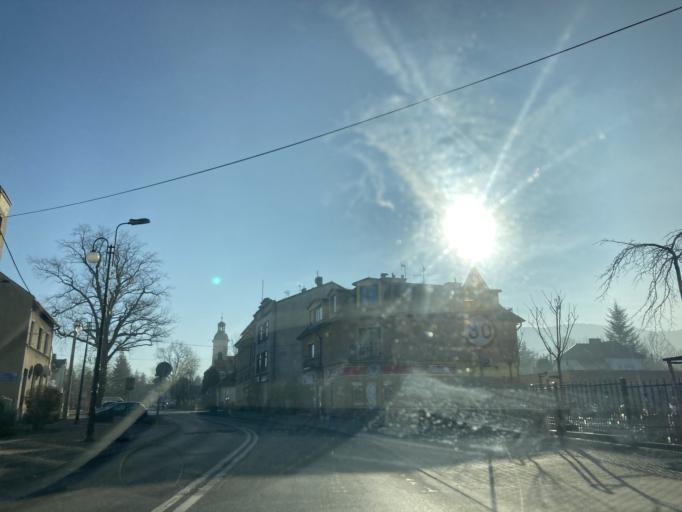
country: PL
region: Silesian Voivodeship
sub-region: Powiat cieszynski
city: Ustron
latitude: 49.7216
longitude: 18.8090
